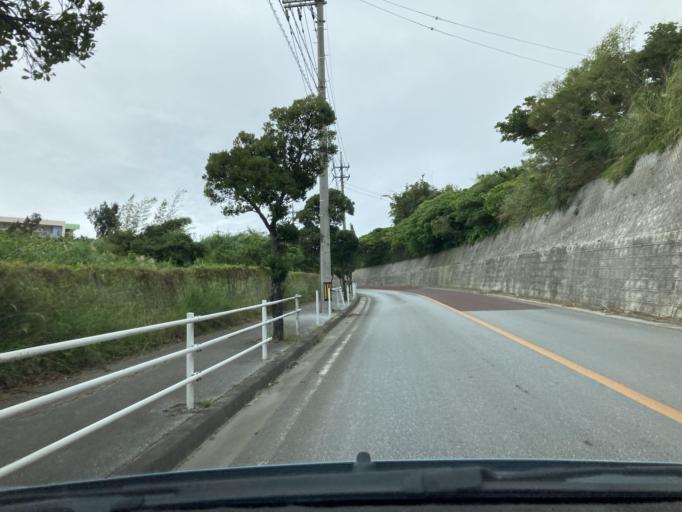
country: JP
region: Okinawa
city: Tomigusuku
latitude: 26.1640
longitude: 127.7087
